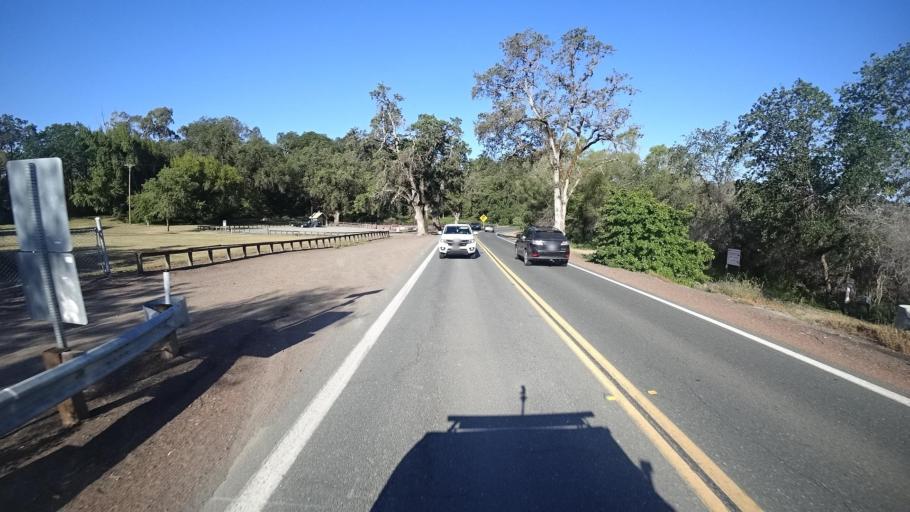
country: US
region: California
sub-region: Lake County
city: North Lakeport
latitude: 39.1181
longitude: -122.8869
